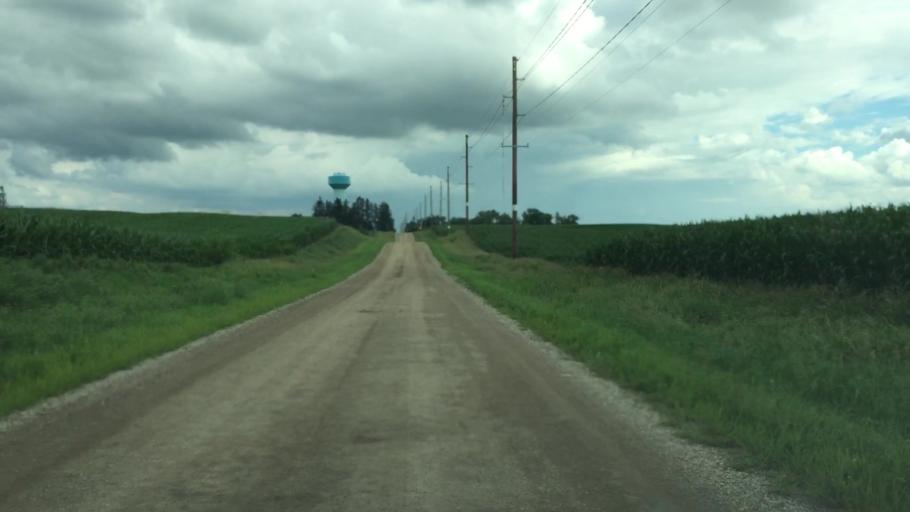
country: US
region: Iowa
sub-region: Jasper County
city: Newton
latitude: 41.7414
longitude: -93.0195
